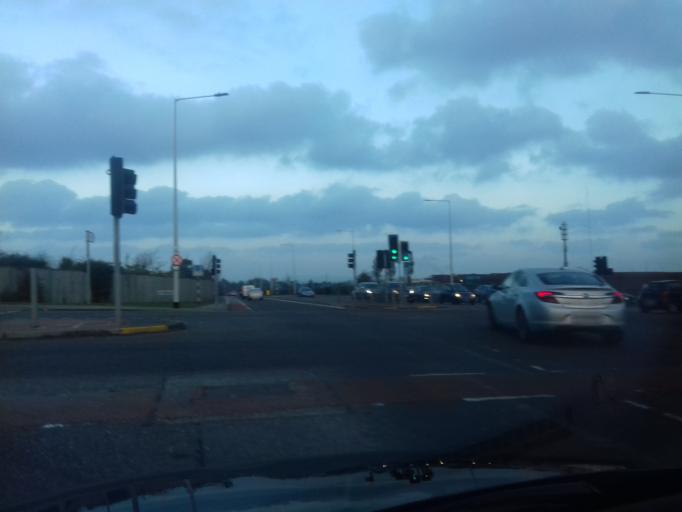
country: IE
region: Leinster
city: Sandyford
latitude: 53.2754
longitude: -6.2234
